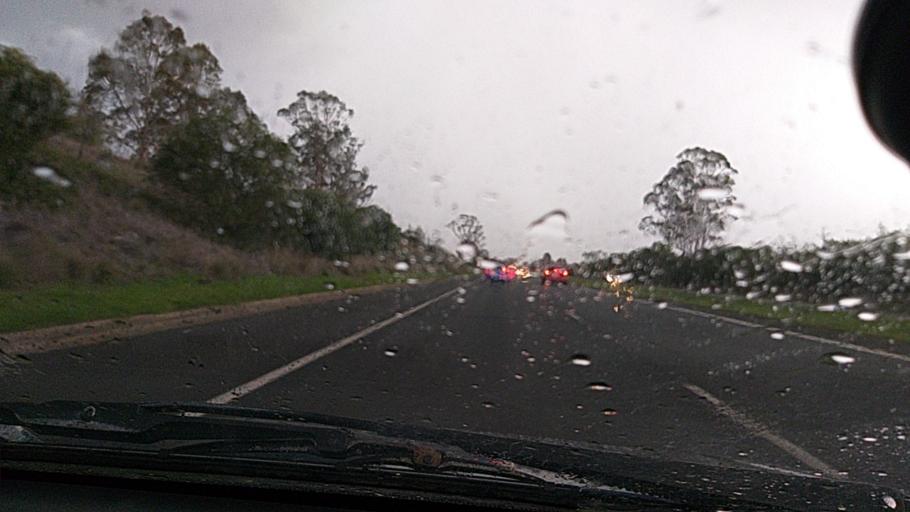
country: AU
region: New South Wales
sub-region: Camden
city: Narellan Vale
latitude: -34.0578
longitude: 150.7318
